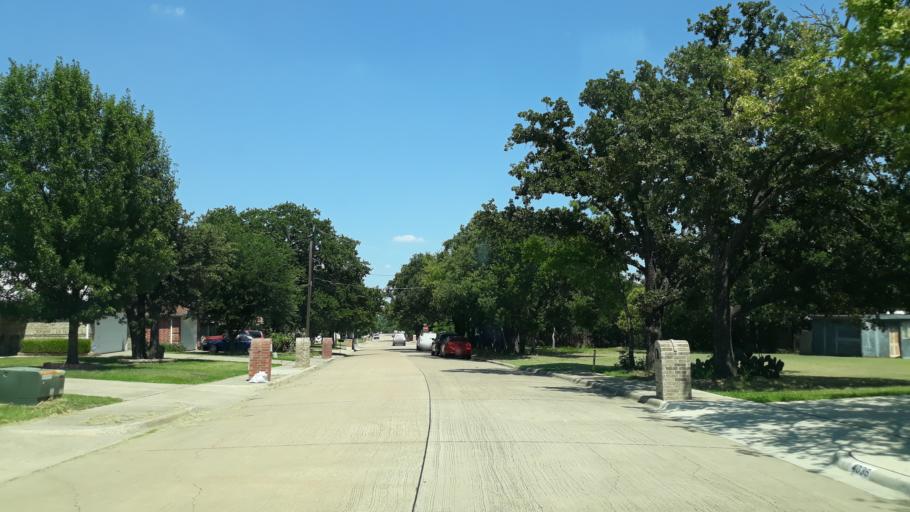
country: US
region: Texas
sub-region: Dallas County
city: Irving
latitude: 32.8235
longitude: -97.0039
